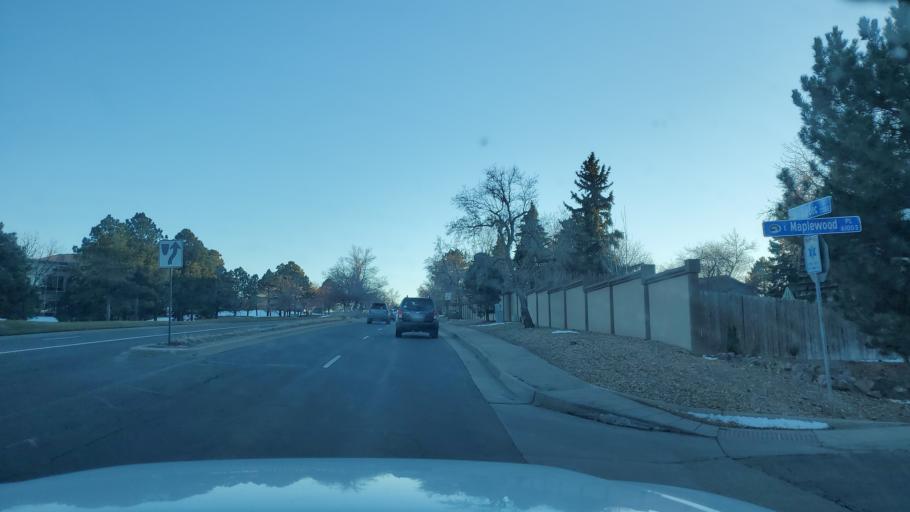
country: US
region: Colorado
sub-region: Arapahoe County
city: Castlewood
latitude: 39.6056
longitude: -104.9042
